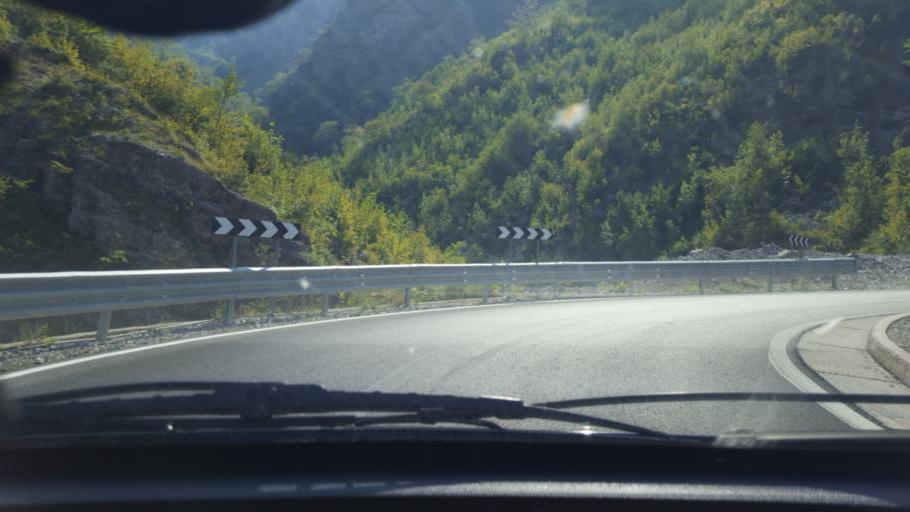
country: AL
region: Shkoder
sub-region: Rrethi i Malesia e Madhe
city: Kastrat
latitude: 42.4127
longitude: 19.5102
